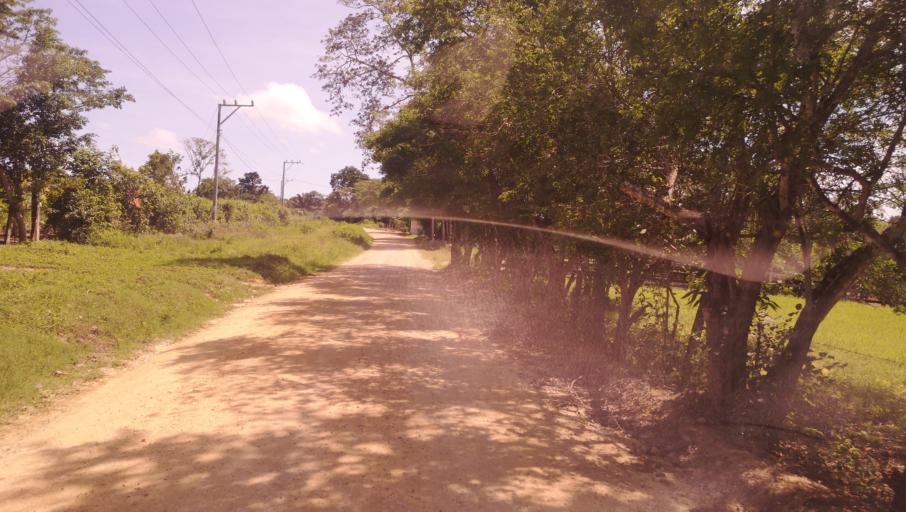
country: GT
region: Peten
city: Melchor de Mencos
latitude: 16.9285
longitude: -89.2786
